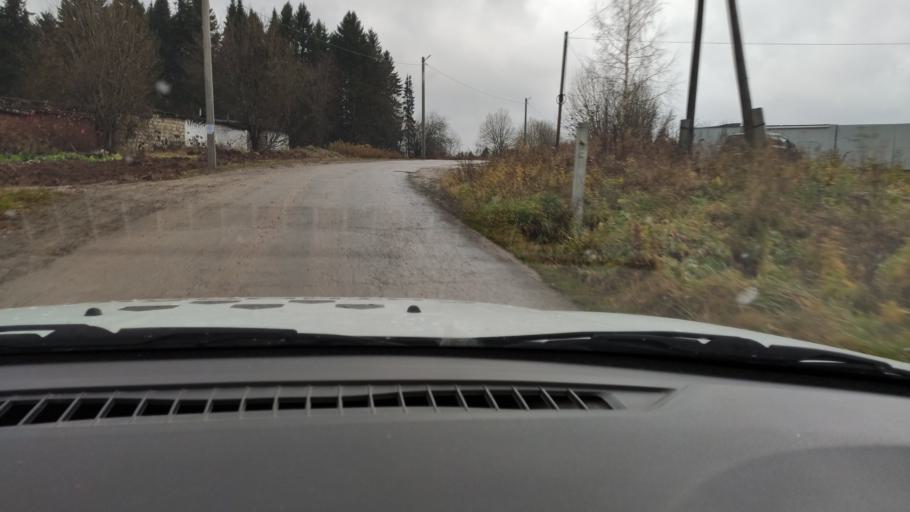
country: RU
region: Perm
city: Sylva
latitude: 58.0401
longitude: 56.7485
